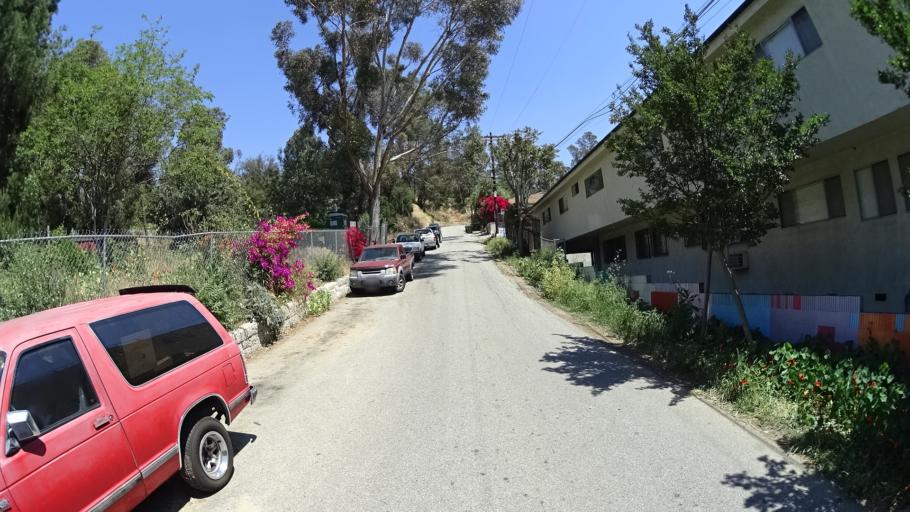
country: US
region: California
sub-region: Los Angeles County
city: Los Angeles
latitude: 34.0750
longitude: -118.2316
